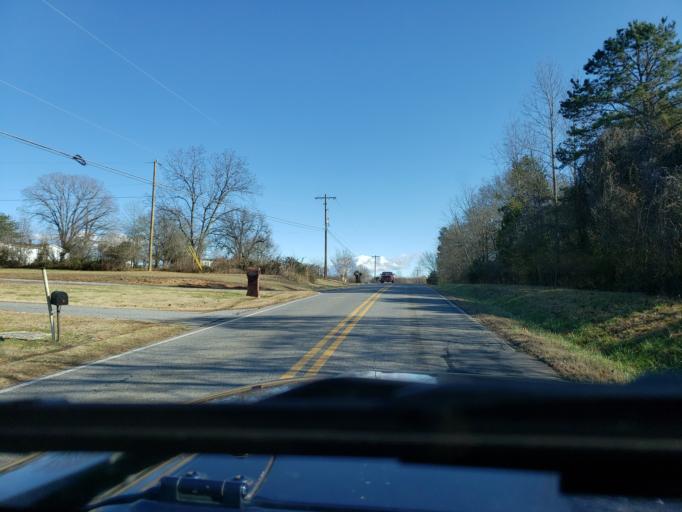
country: US
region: South Carolina
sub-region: Cherokee County
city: Blacksburg
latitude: 35.1905
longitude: -81.4714
